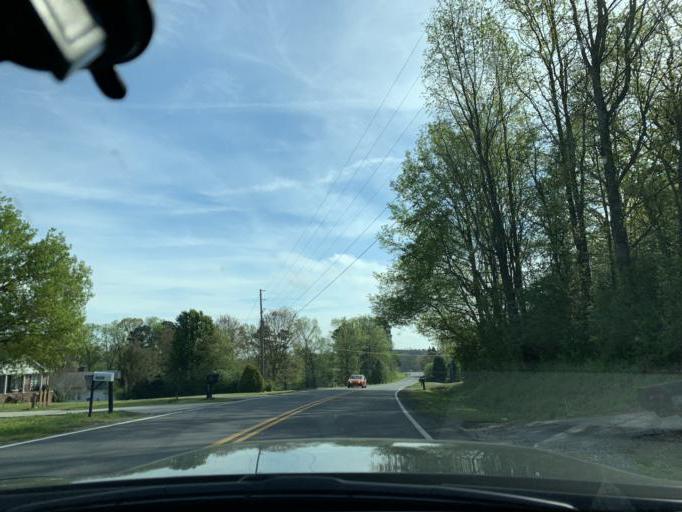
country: US
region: Georgia
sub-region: Forsyth County
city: Cumming
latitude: 34.2568
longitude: -84.1379
